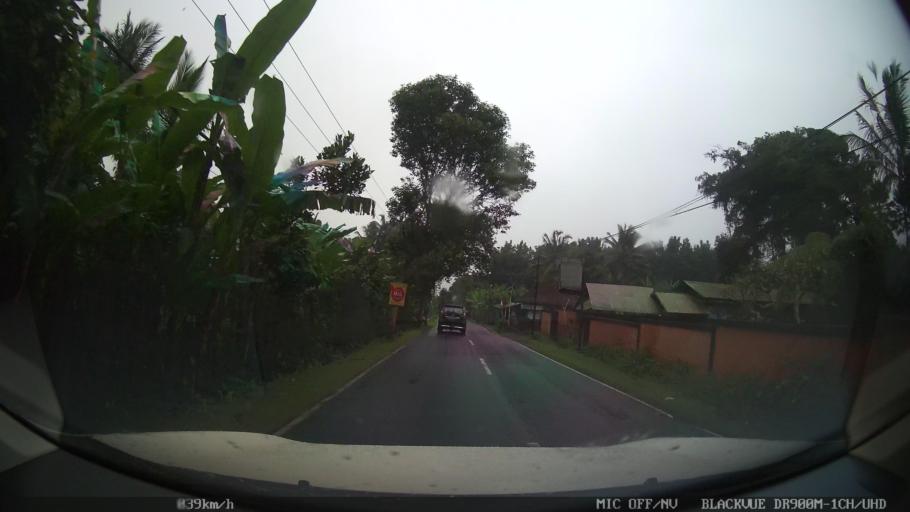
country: ID
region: Bali
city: Banjar Taro Kelod
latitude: -8.3726
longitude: 115.2686
